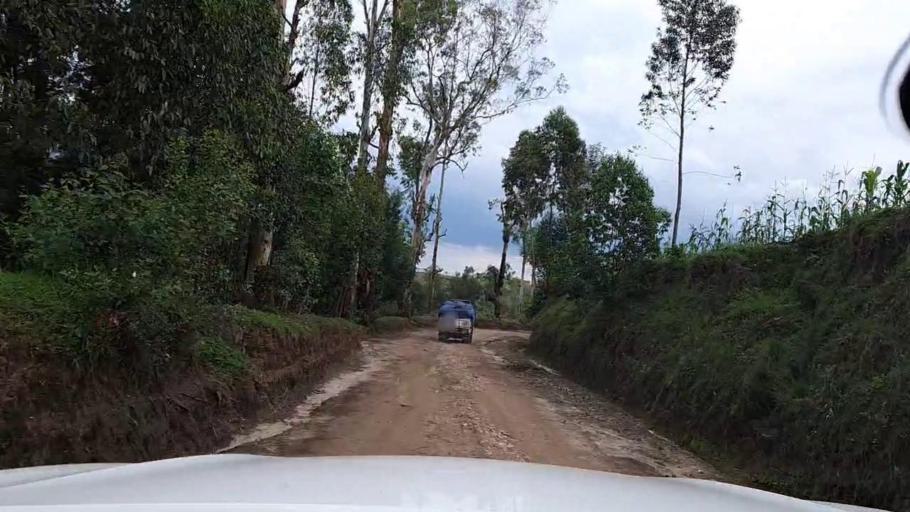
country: BI
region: Kayanza
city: Kayanza
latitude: -2.7981
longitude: 29.4993
